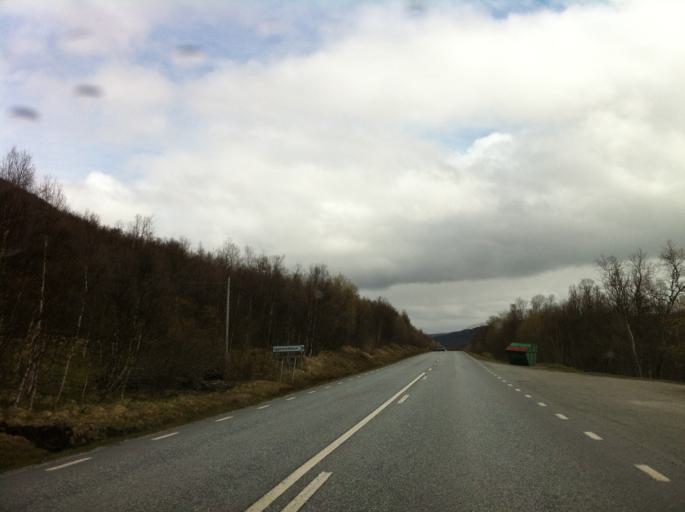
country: NO
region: Sor-Trondelag
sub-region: Tydal
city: Aas
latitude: 62.5655
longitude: 12.2510
